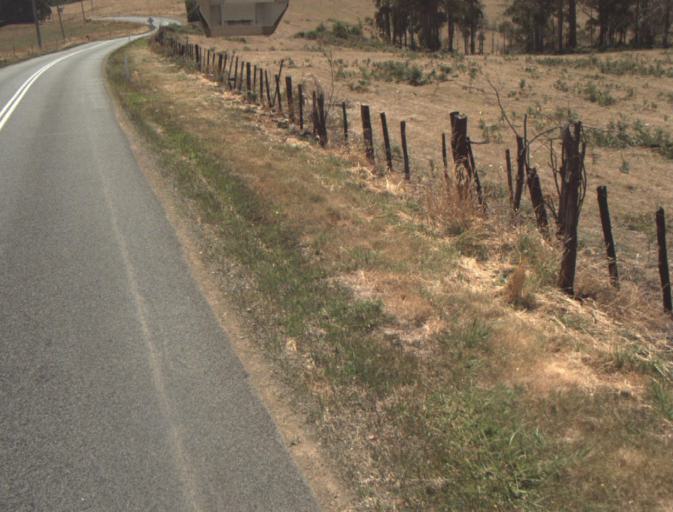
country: AU
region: Tasmania
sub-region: Launceston
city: Mayfield
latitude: -41.2717
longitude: 147.1282
